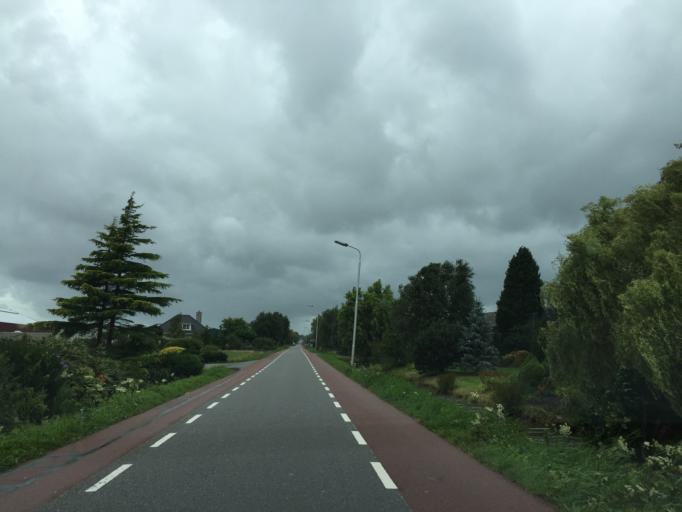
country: NL
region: South Holland
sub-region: Gemeente Pijnacker-Nootdorp
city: Pijnacker
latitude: 52.0394
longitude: 4.4244
